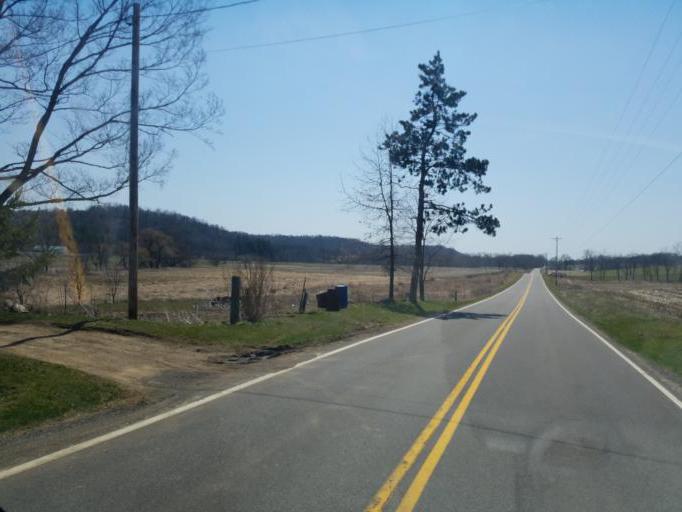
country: US
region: Ohio
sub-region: Ashland County
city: Loudonville
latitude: 40.7123
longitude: -82.2869
